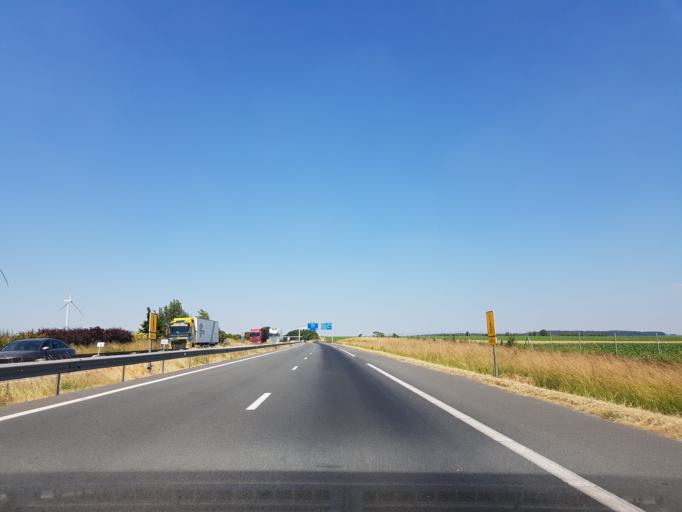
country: FR
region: Nord-Pas-de-Calais
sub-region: Departement du Nord
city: Marcoing
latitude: 50.1312
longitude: 3.1470
